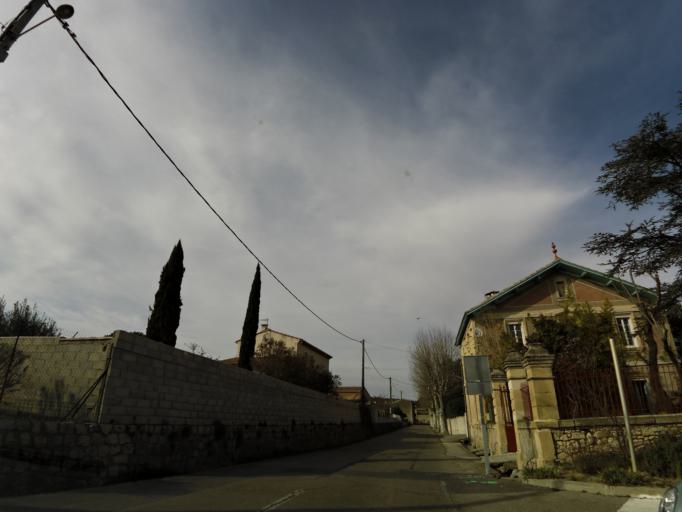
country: FR
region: Languedoc-Roussillon
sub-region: Departement du Gard
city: Congenies
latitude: 43.7742
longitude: 4.1590
